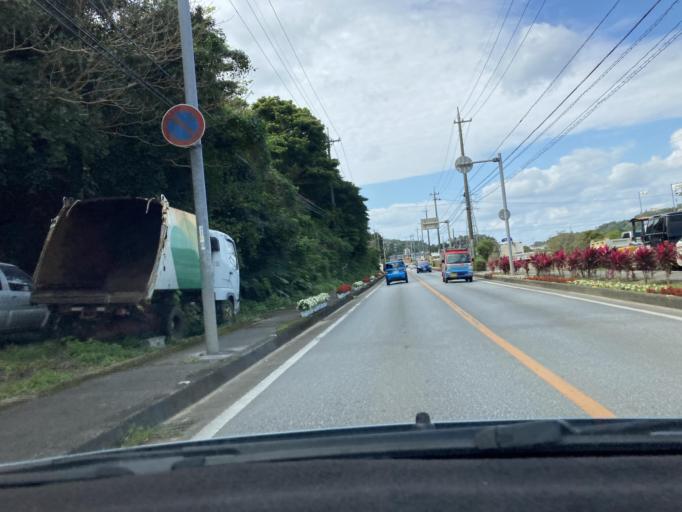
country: JP
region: Okinawa
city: Nago
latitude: 26.6568
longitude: 127.9097
